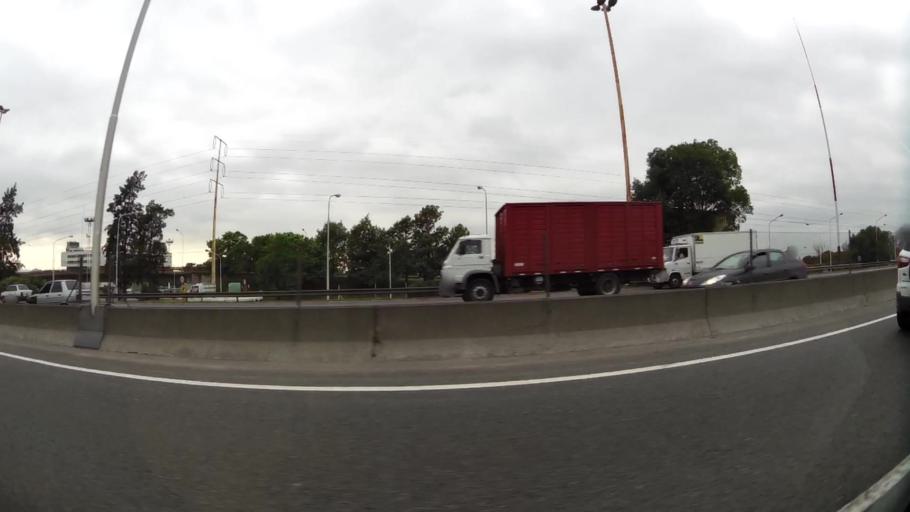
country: AR
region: Buenos Aires F.D.
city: Villa Lugano
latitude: -34.7095
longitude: -58.5041
